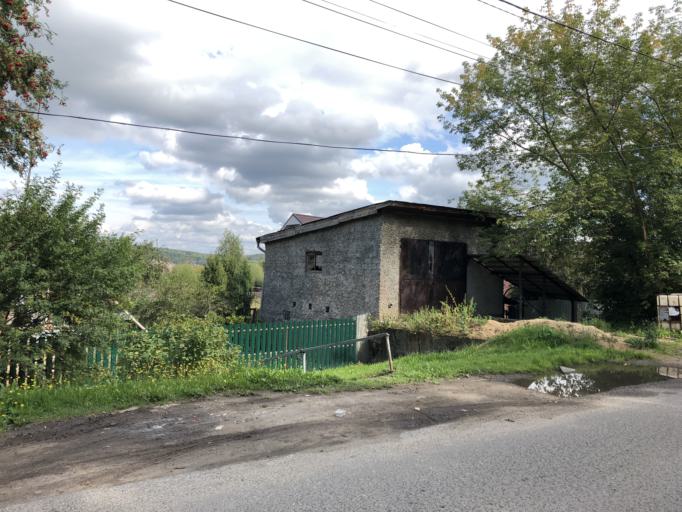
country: RU
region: Moskovskaya
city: Yakhroma
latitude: 56.2931
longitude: 37.4731
